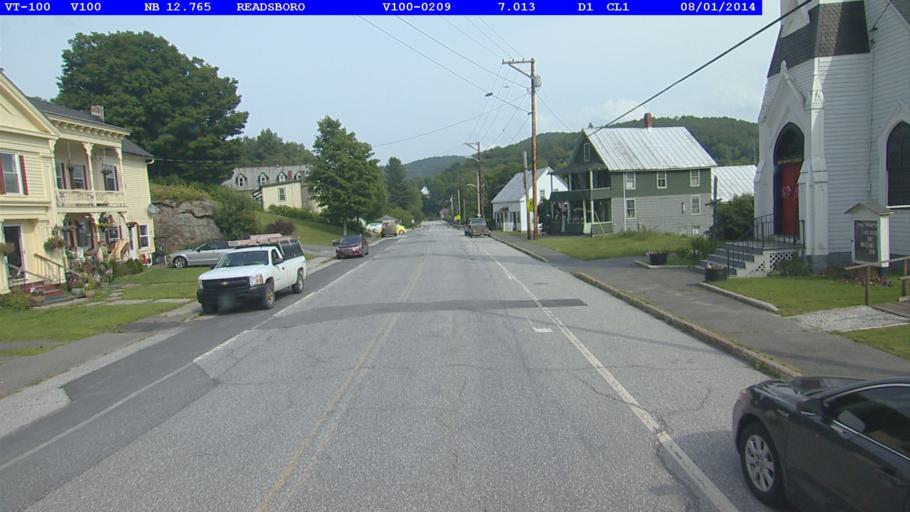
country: US
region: Massachusetts
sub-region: Franklin County
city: Charlemont
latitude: 42.7721
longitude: -72.9482
